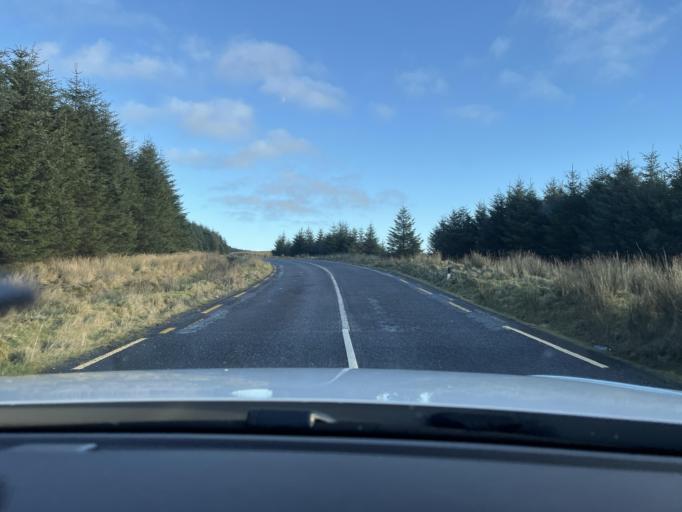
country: IE
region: Ulster
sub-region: An Cabhan
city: Ballyconnell
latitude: 54.1702
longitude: -7.8354
